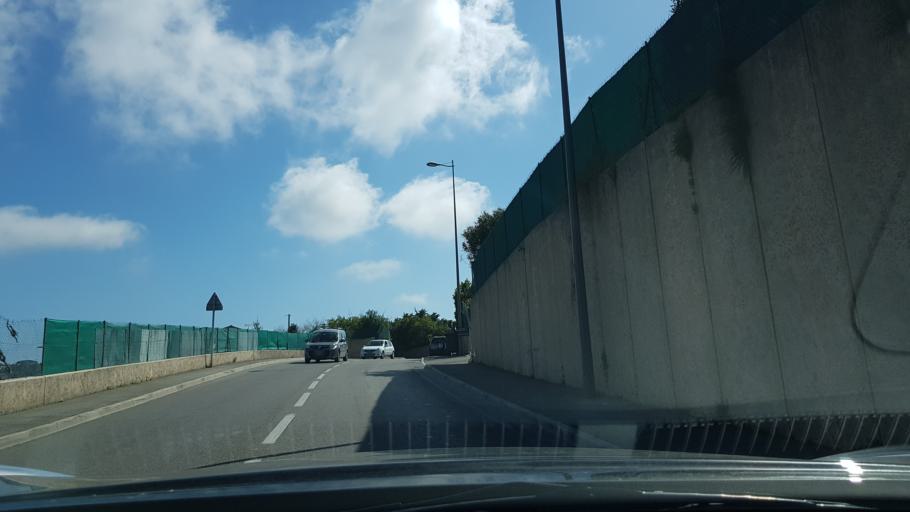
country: FR
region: Provence-Alpes-Cote d'Azur
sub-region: Departement des Alpes-Maritimes
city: Vallauris
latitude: 43.5815
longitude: 7.0509
